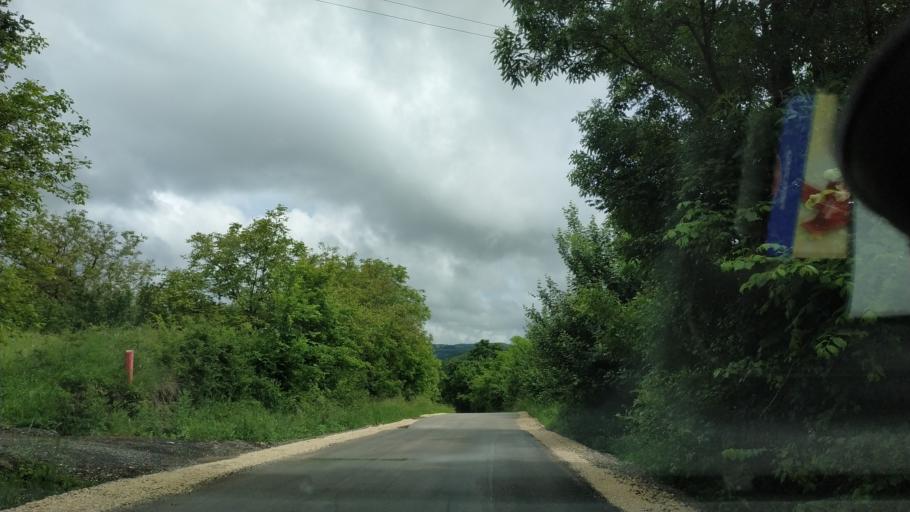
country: RS
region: Central Serbia
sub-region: Zajecarski Okrug
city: Soko Banja
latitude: 43.6529
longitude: 21.9028
